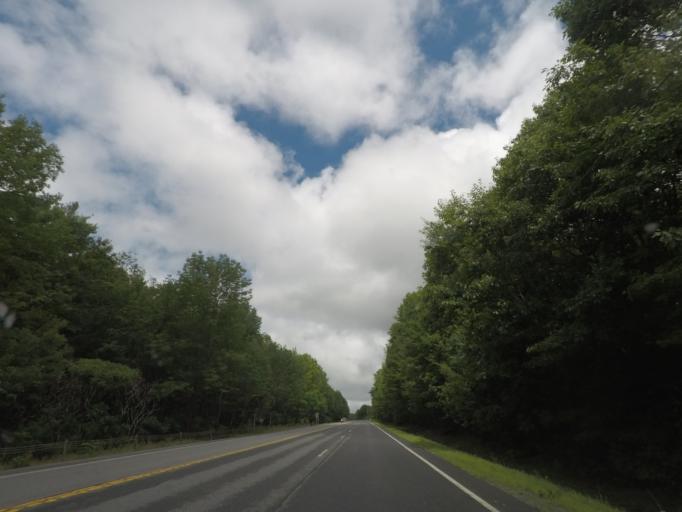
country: US
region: Massachusetts
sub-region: Berkshire County
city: Lanesborough
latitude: 42.5759
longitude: -73.3677
